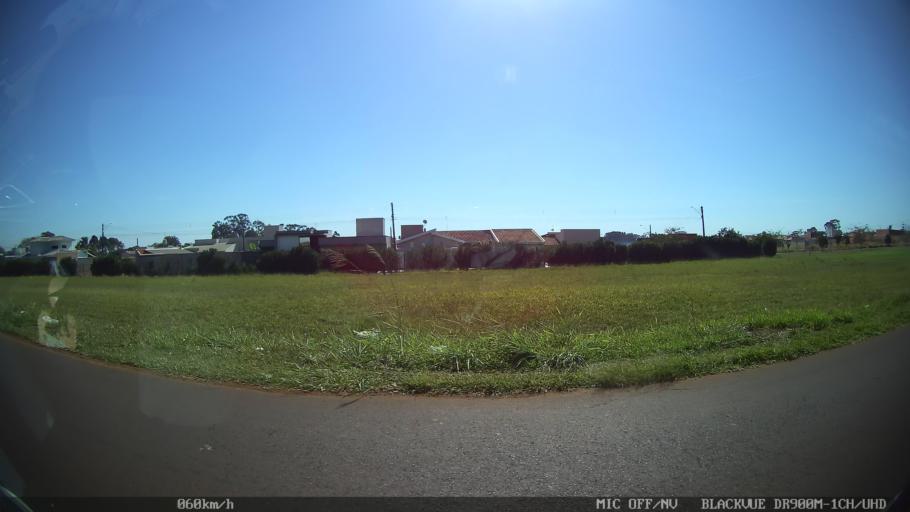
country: BR
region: Sao Paulo
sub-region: Batatais
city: Batatais
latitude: -20.8750
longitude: -47.5883
